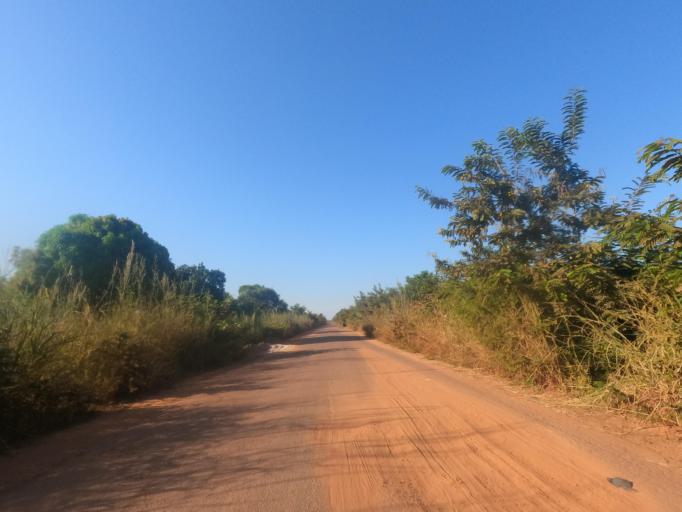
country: GW
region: Cacheu
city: Cacheu
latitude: 12.4217
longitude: -16.2034
